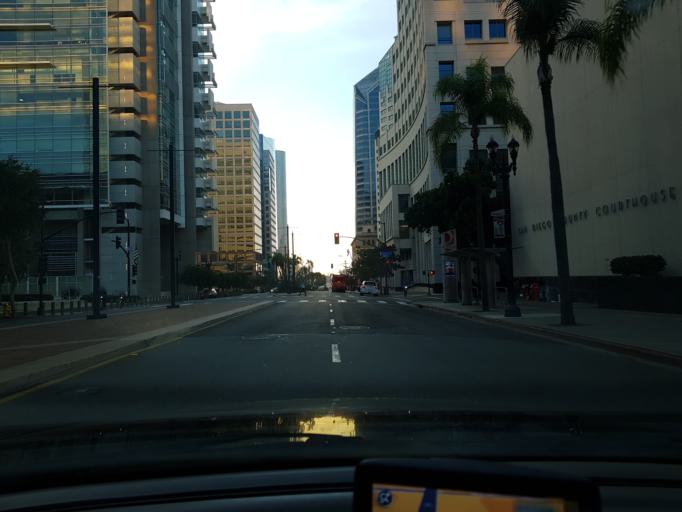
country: US
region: California
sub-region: San Diego County
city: San Diego
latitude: 32.7158
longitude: -117.1651
